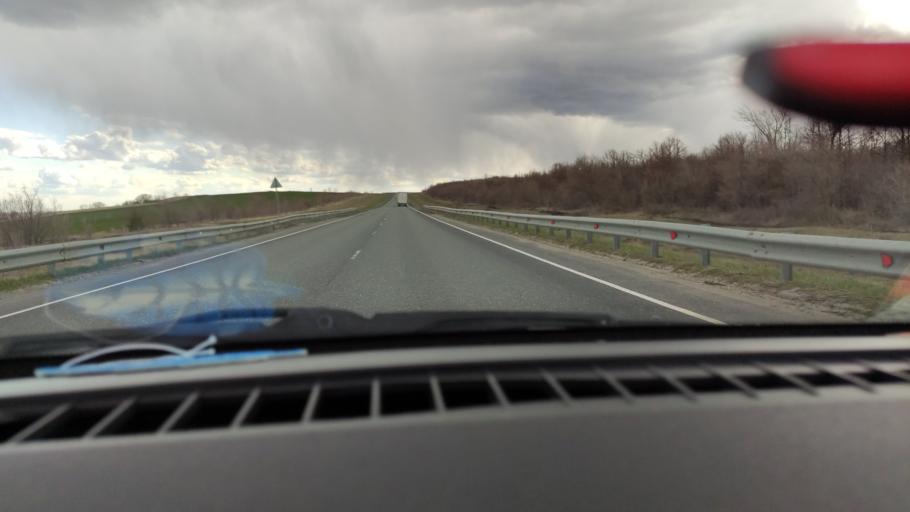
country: RU
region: Saratov
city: Balakovo
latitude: 52.1941
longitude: 47.8566
